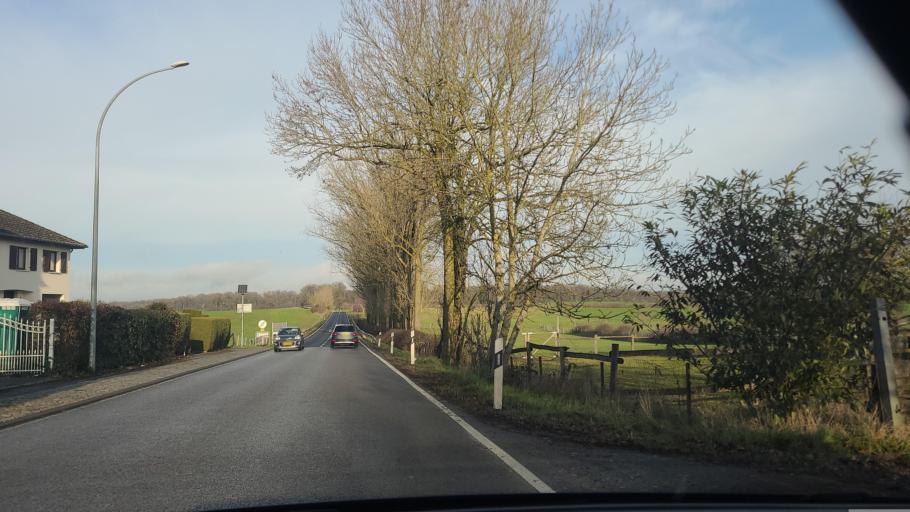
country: LU
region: Luxembourg
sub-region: Canton de Capellen
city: Koerich
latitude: 49.6483
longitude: 5.9555
